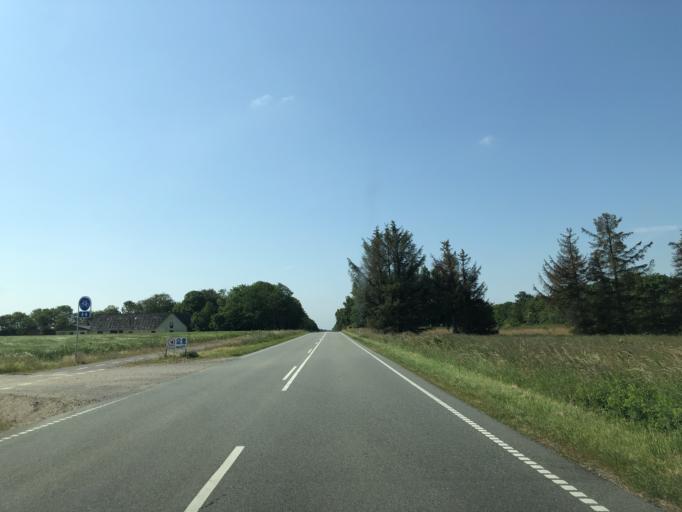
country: DK
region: South Denmark
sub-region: Varde Kommune
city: Varde
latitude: 55.6515
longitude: 8.4884
